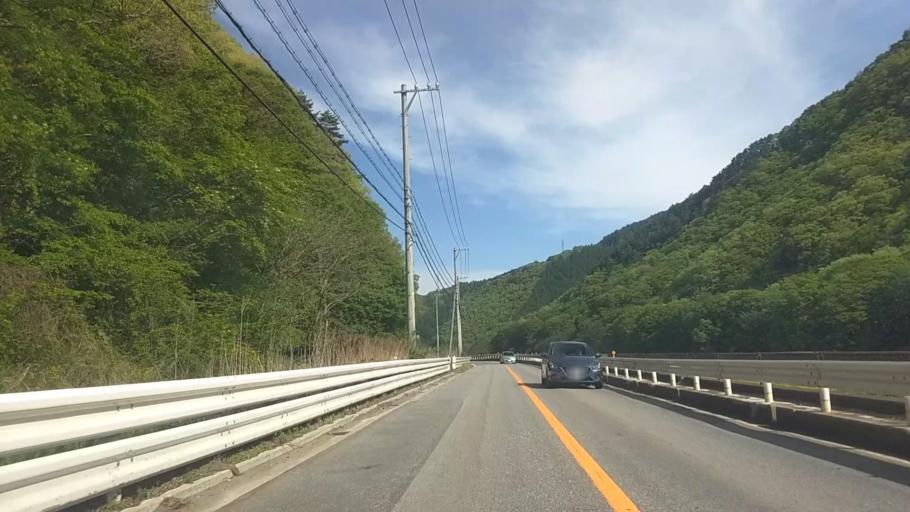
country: JP
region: Nagano
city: Saku
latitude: 36.0308
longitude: 138.4857
